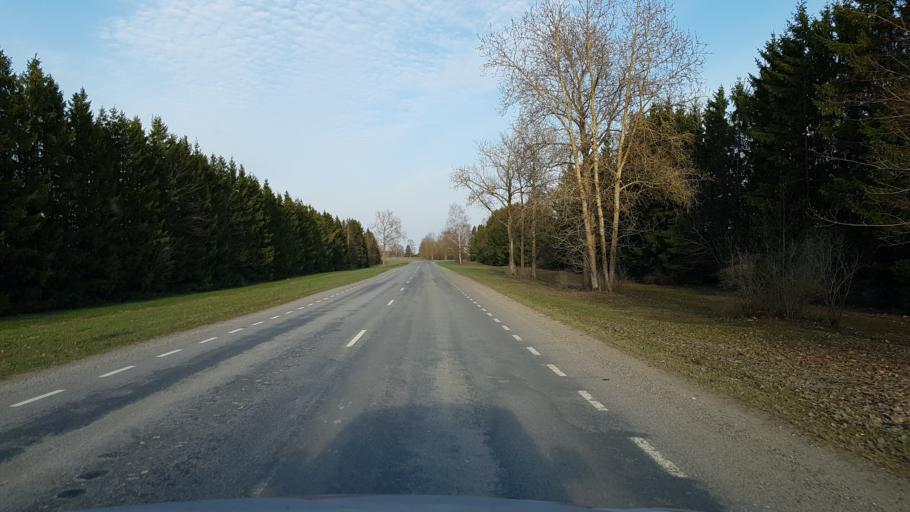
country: EE
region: Laeaene-Virumaa
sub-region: Someru vald
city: Someru
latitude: 59.3647
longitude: 26.4172
